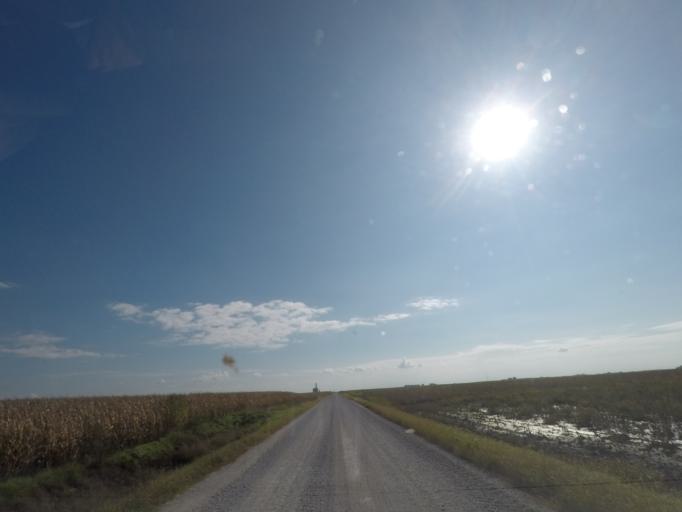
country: US
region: Iowa
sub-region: Story County
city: Nevada
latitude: 42.0490
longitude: -93.4308
